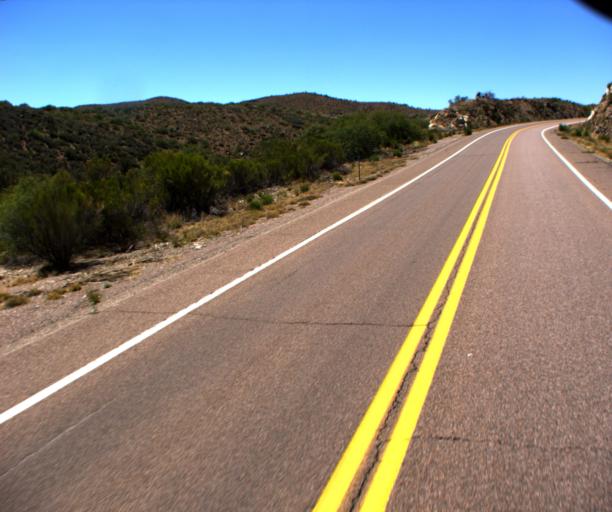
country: US
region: Arizona
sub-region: Yavapai County
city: Bagdad
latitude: 34.5483
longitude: -113.1495
